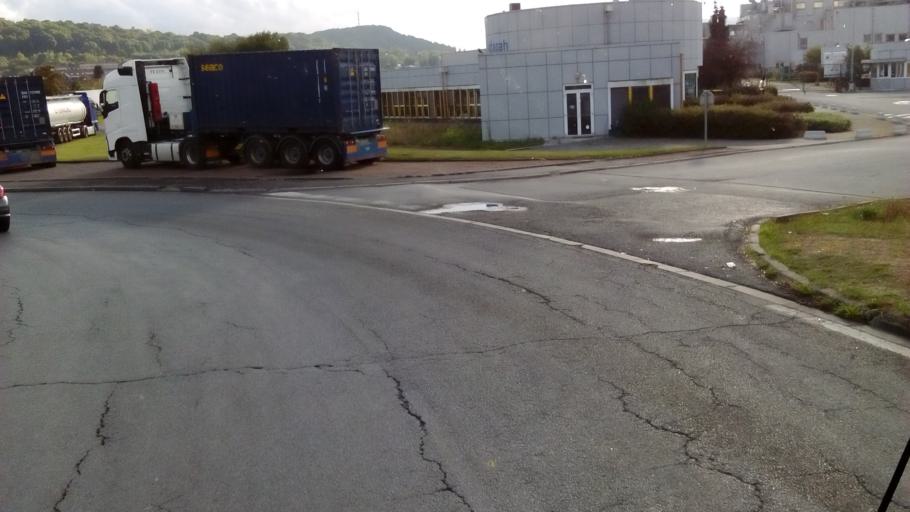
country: FR
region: Lorraine
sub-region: Departement de Meurthe-et-Moselle
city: Longlaville
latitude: 49.5409
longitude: 5.8076
